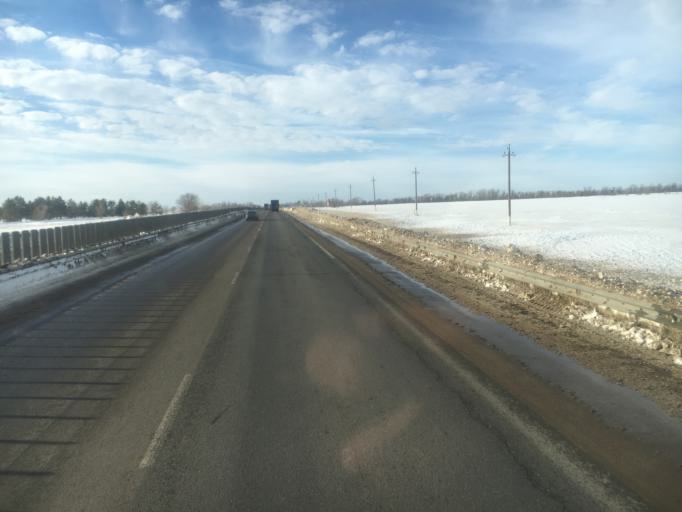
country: RU
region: Samara
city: Mirnyy
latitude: 53.4618
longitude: 50.2056
